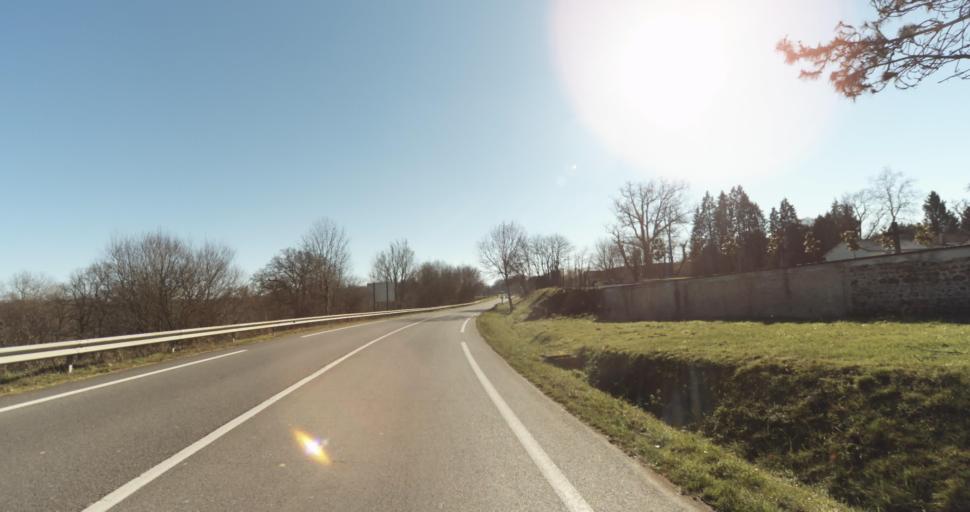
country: FR
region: Aquitaine
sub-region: Departement des Pyrenees-Atlantiques
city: Morlaas
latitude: 43.3496
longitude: -0.2557
